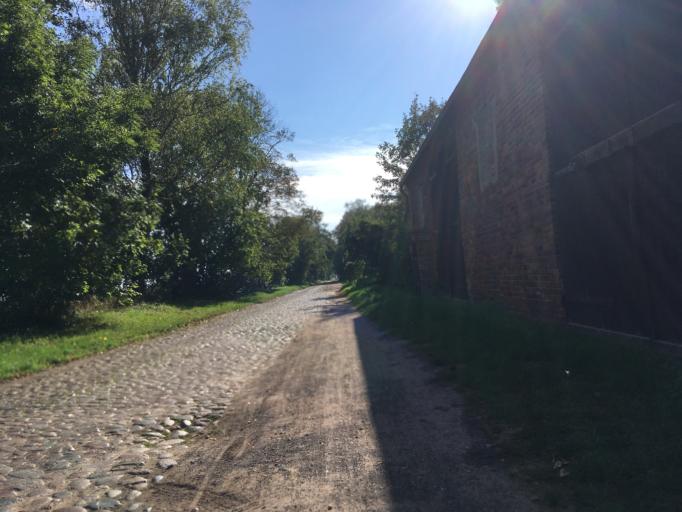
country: DE
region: Brandenburg
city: Altlandsberg
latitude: 52.5637
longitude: 13.7312
